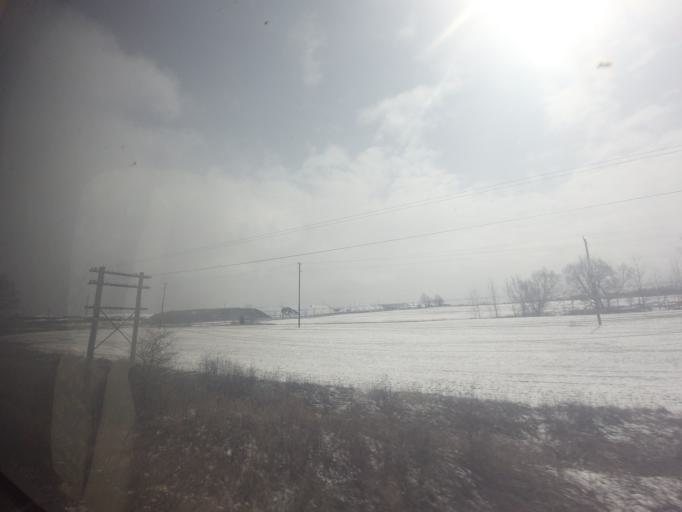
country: CA
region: Ontario
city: Cobourg
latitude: 43.9172
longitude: -78.4630
